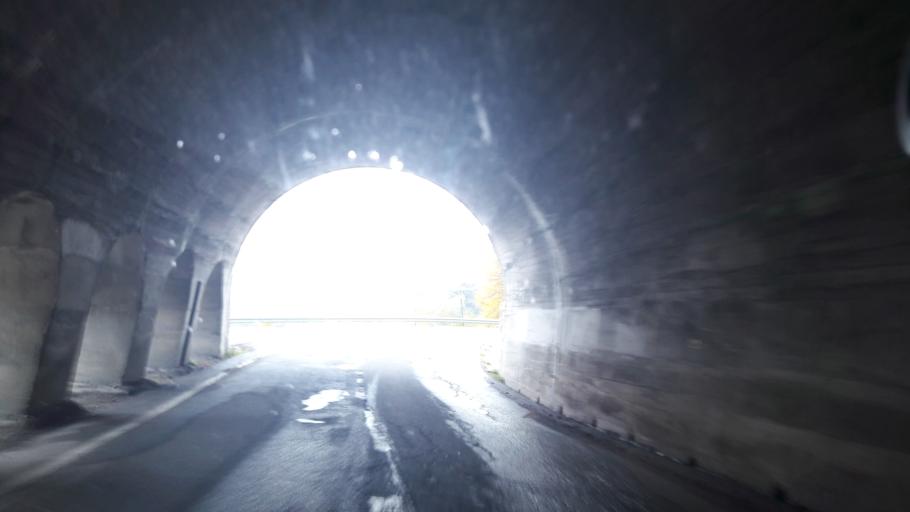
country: FR
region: Rhone-Alpes
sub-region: Departement de la Savoie
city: Tignes
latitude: 45.4809
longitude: 6.9234
